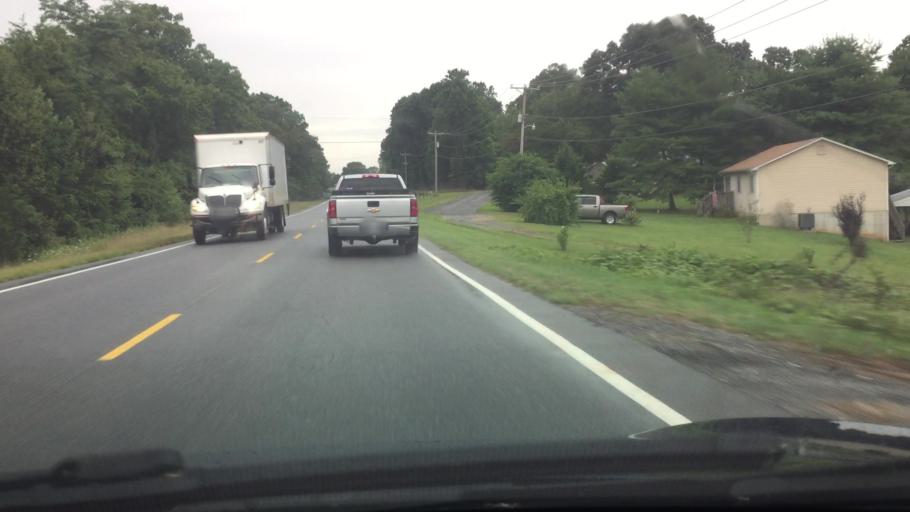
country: US
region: Virginia
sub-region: City of Bedford
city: Bedford
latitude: 37.3634
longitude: -79.4449
